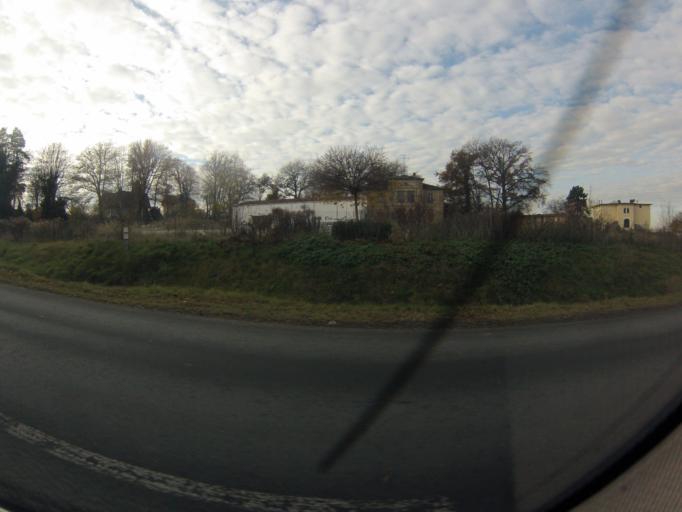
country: DE
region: Saxony
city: Meerane
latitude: 50.8525
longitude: 12.4468
